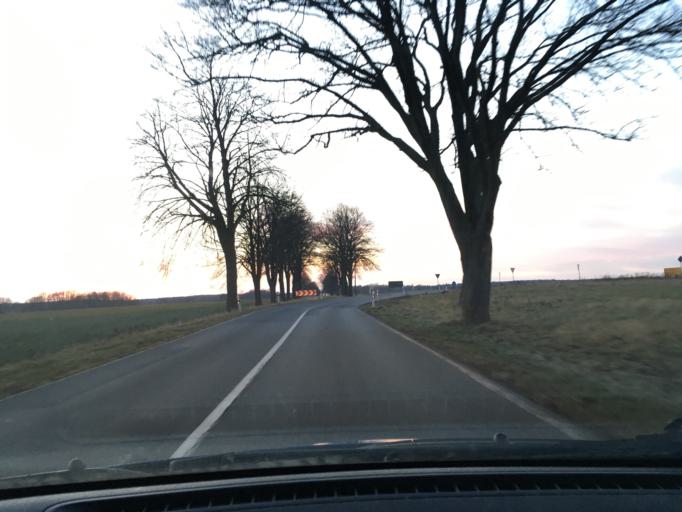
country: DE
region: Lower Saxony
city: Dahlenburg
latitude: 53.1891
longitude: 10.7110
